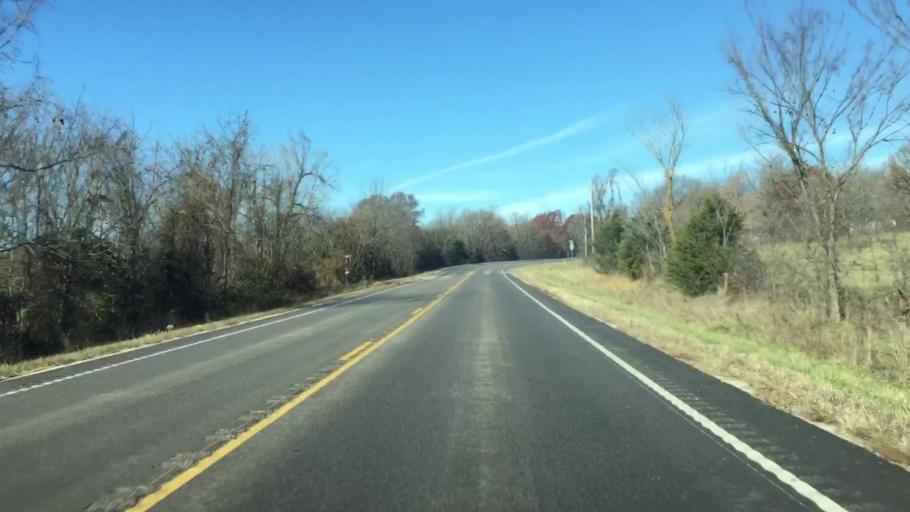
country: US
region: Missouri
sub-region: Miller County
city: Eldon
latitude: 38.3641
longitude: -92.6120
